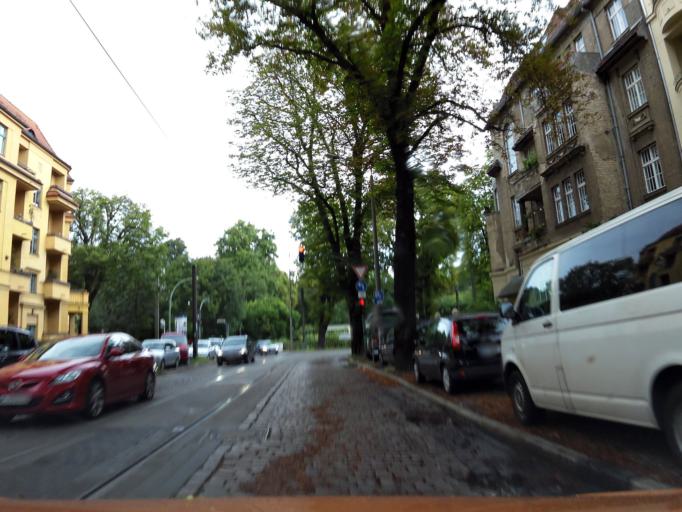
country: DE
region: Brandenburg
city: Potsdam
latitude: 52.3931
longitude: 13.0276
